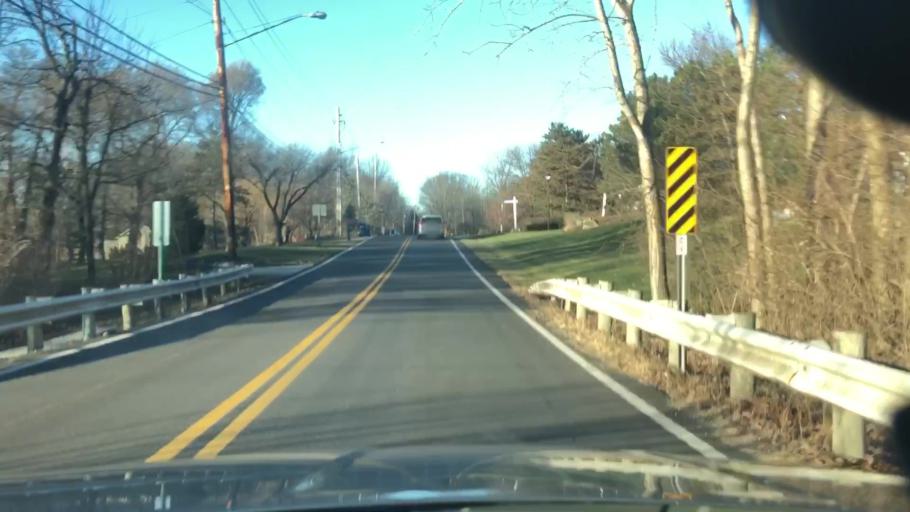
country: US
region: Ohio
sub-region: Cuyahoga County
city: Olmsted Falls
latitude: 41.3663
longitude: -81.8952
